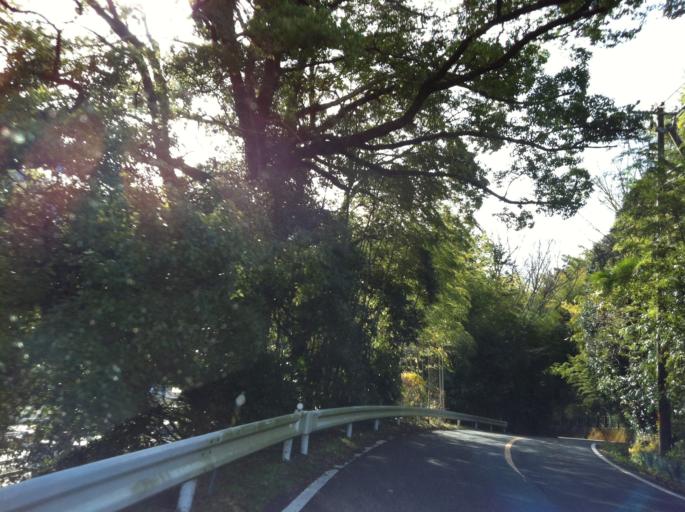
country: JP
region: Shizuoka
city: Yaizu
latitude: 34.9264
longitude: 138.3015
